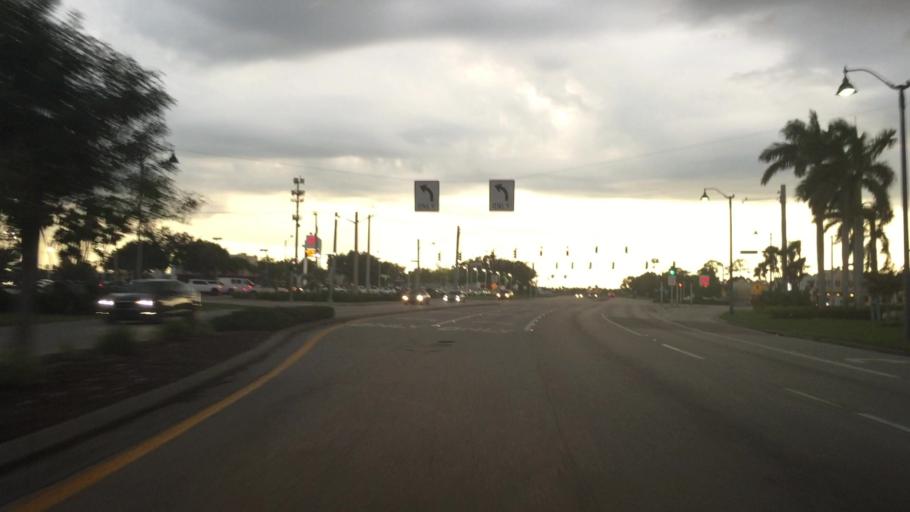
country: US
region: Florida
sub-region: Lee County
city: Pine Manor
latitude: 26.5982
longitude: -81.8621
